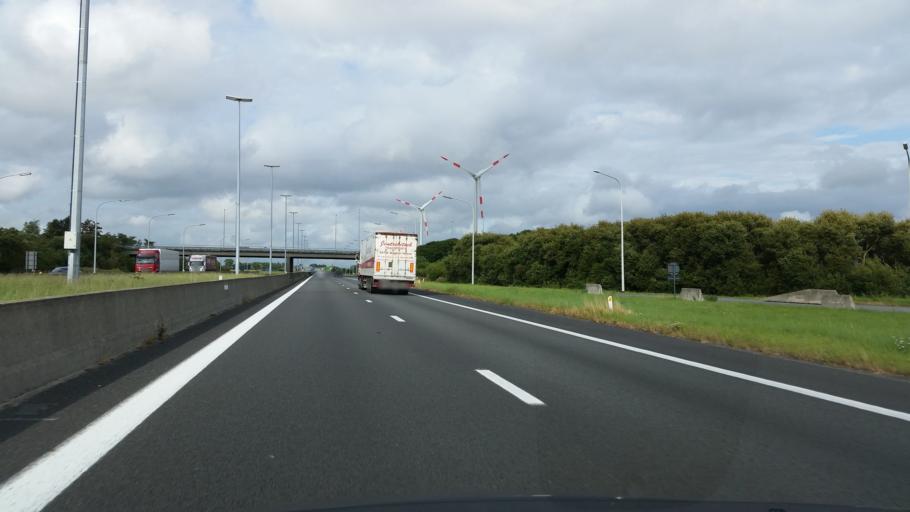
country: BE
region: Flanders
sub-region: Provincie West-Vlaanderen
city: Gistel
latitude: 51.1581
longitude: 2.9355
